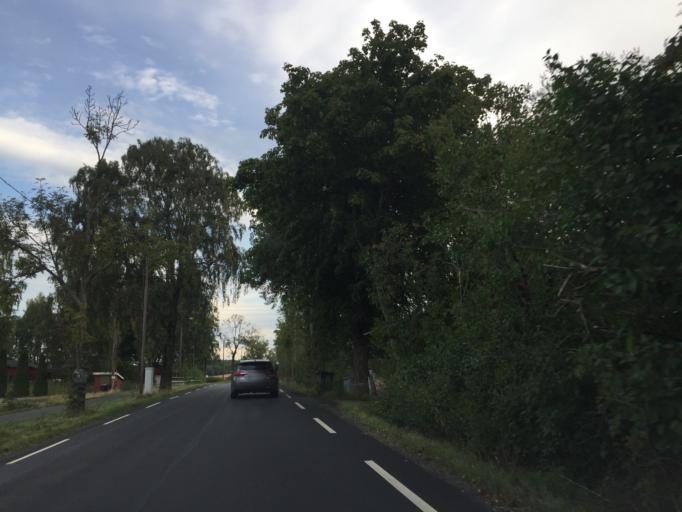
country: NO
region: Akershus
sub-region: As
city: As
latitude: 59.7092
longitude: 10.7720
